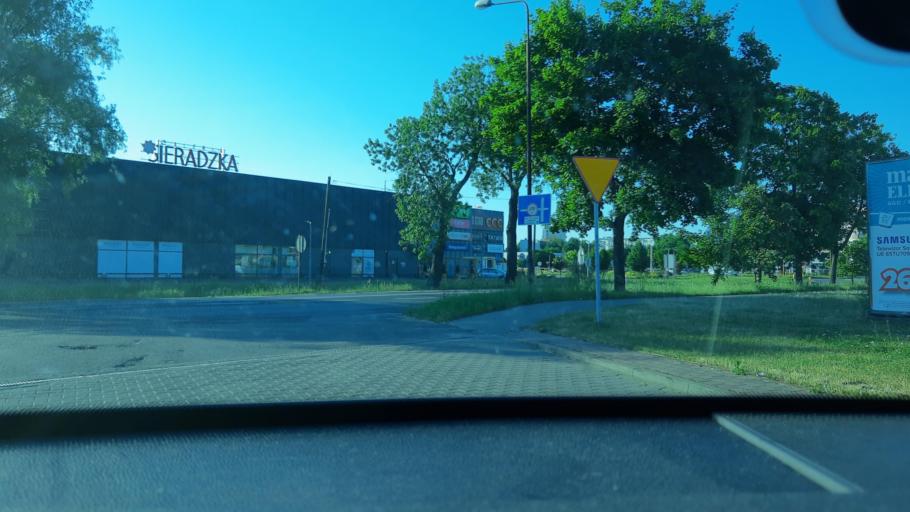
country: PL
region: Lodz Voivodeship
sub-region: Powiat sieradzki
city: Sieradz
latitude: 51.5853
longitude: 18.7236
